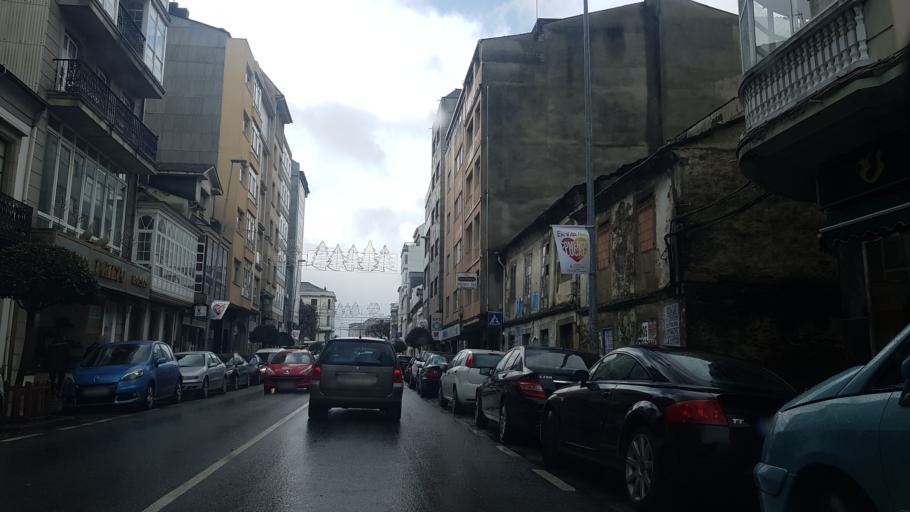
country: ES
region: Galicia
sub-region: Provincia de Lugo
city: Vilalba
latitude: 43.2989
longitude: -7.6797
